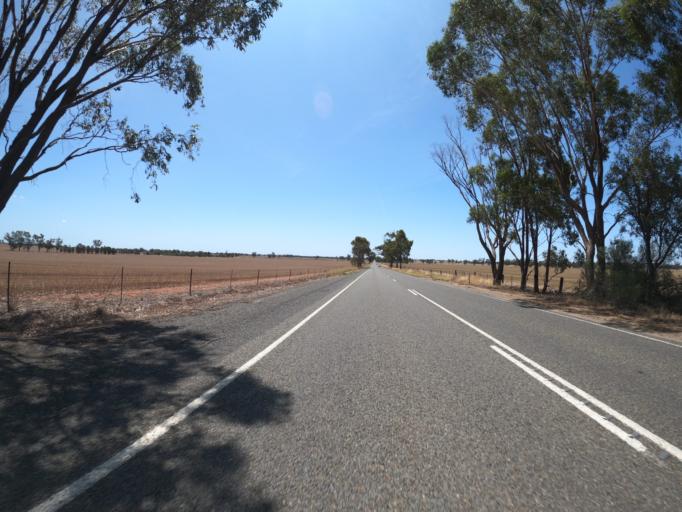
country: AU
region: Victoria
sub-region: Moira
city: Yarrawonga
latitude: -36.0783
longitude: 145.9954
